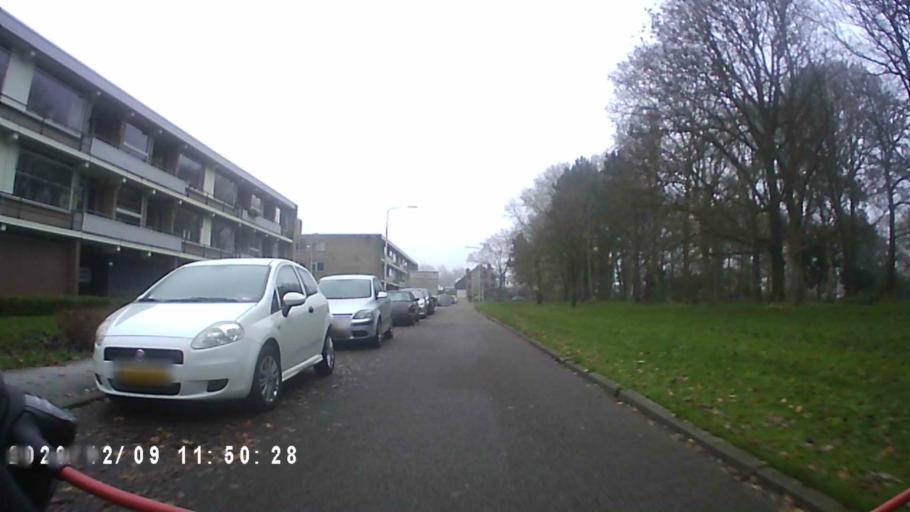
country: NL
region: Groningen
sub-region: Gemeente Haren
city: Haren
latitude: 53.1737
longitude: 6.5981
